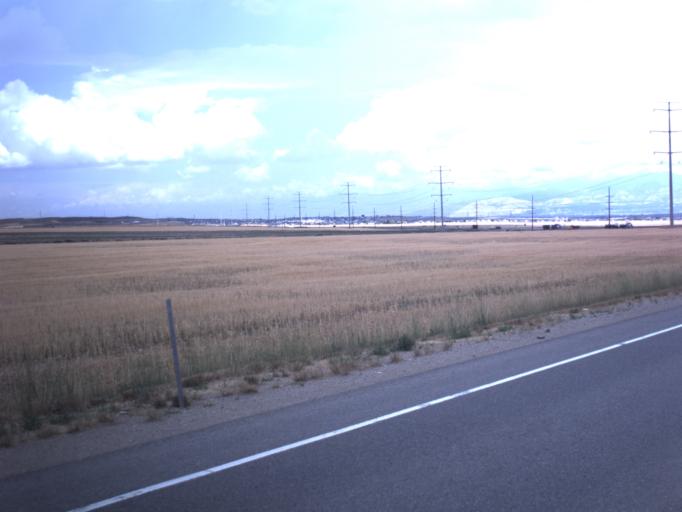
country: US
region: Utah
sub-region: Salt Lake County
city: Oquirrh
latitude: 40.5744
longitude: -112.0649
